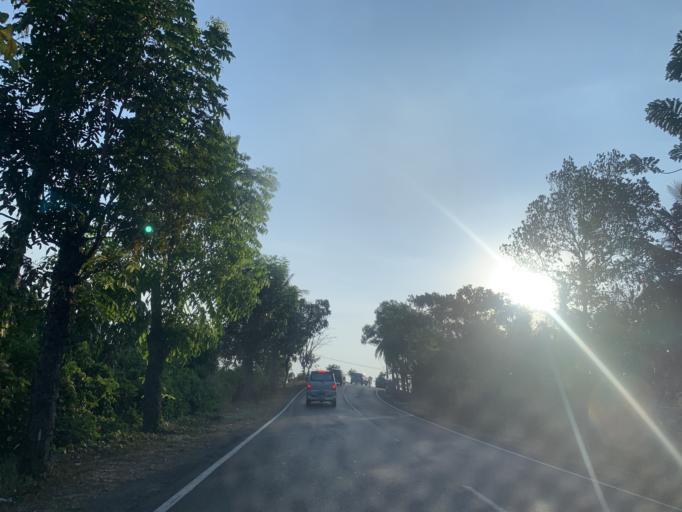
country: ID
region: Bali
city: Angkahgede
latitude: -8.4853
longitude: 114.9462
